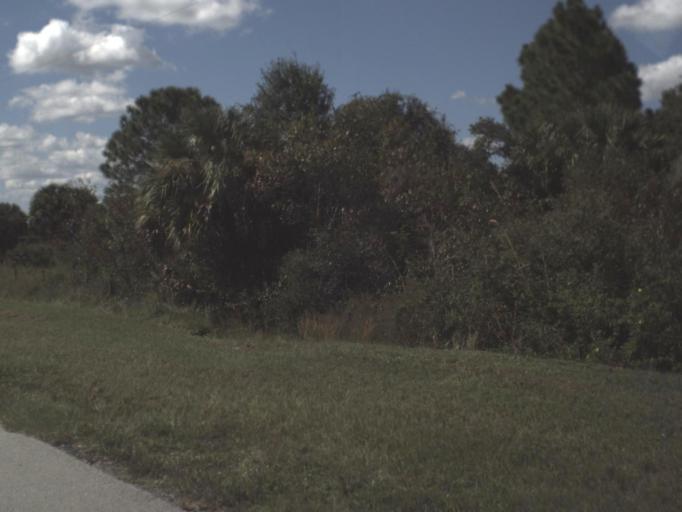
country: US
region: Florida
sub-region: Hendry County
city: Port LaBelle
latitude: 26.8128
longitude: -81.3576
